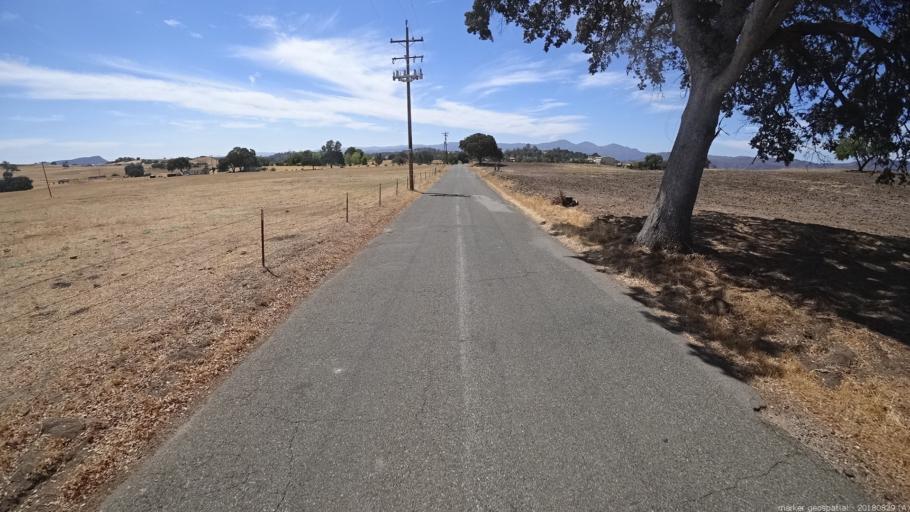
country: US
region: California
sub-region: San Luis Obispo County
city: Lake Nacimiento
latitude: 35.8164
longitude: -121.0576
